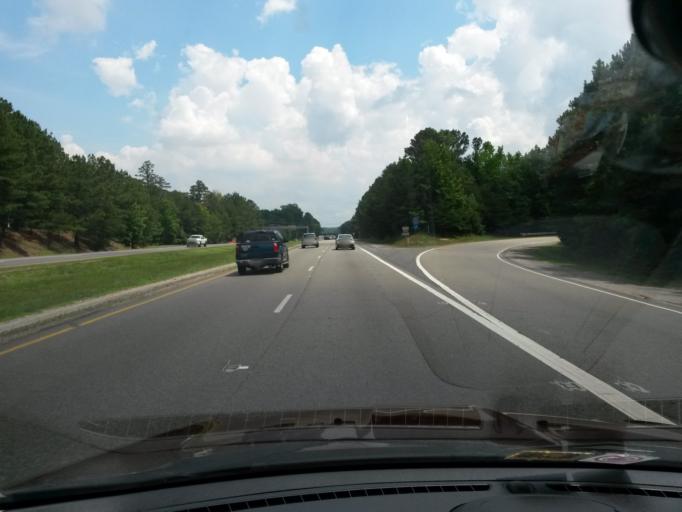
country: US
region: Virginia
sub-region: Chesterfield County
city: Enon
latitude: 37.3411
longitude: -77.3336
